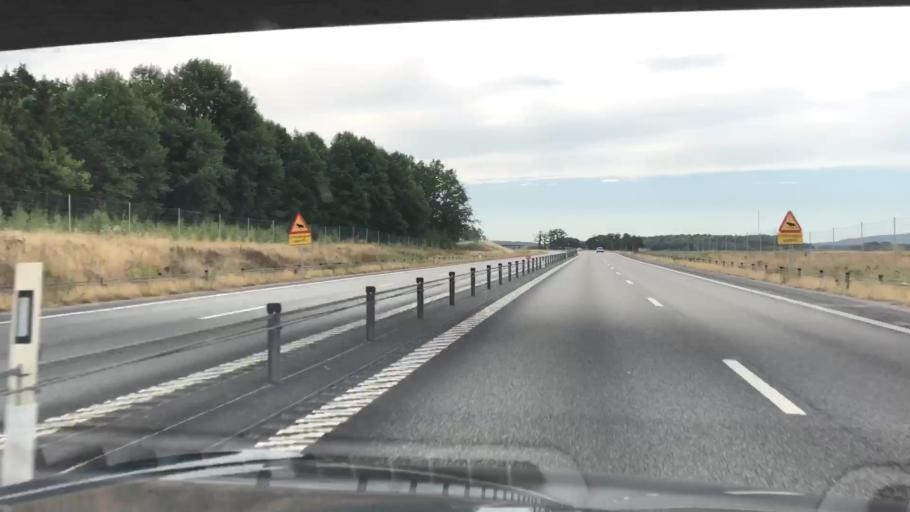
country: SE
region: Blekinge
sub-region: Karlshamns Kommun
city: Morrum
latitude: 56.1402
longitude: 14.6616
